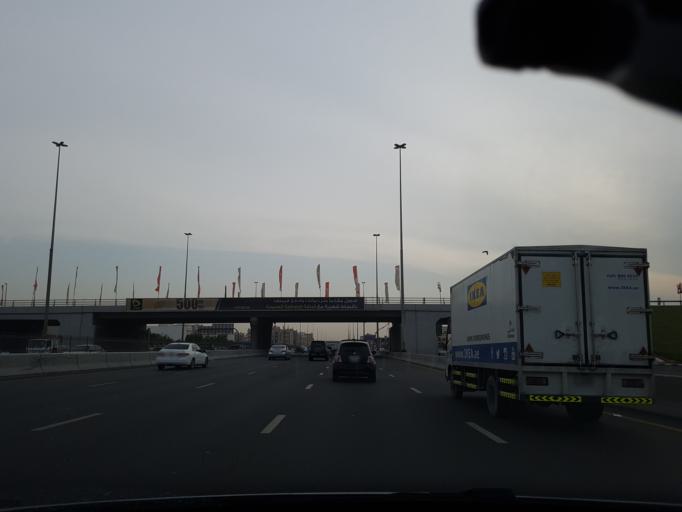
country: AE
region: Ash Shariqah
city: Sharjah
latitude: 25.3170
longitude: 55.4519
